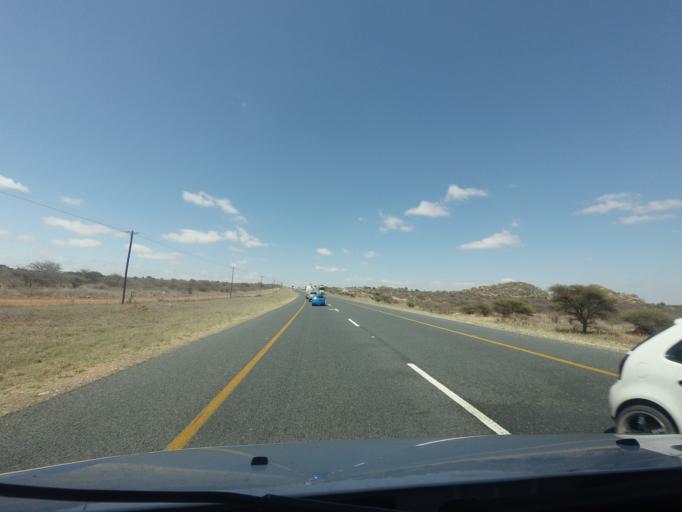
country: ZA
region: Limpopo
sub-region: Vhembe District Municipality
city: Louis Trichardt
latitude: -23.4303
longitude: 29.7480
